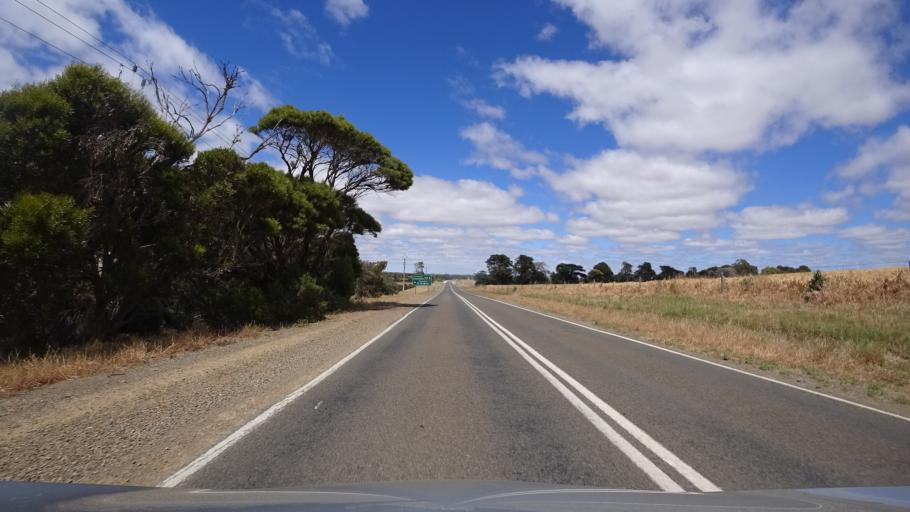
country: AU
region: South Australia
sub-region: Kangaroo Island
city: Kingscote
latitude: -35.6714
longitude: 137.5922
